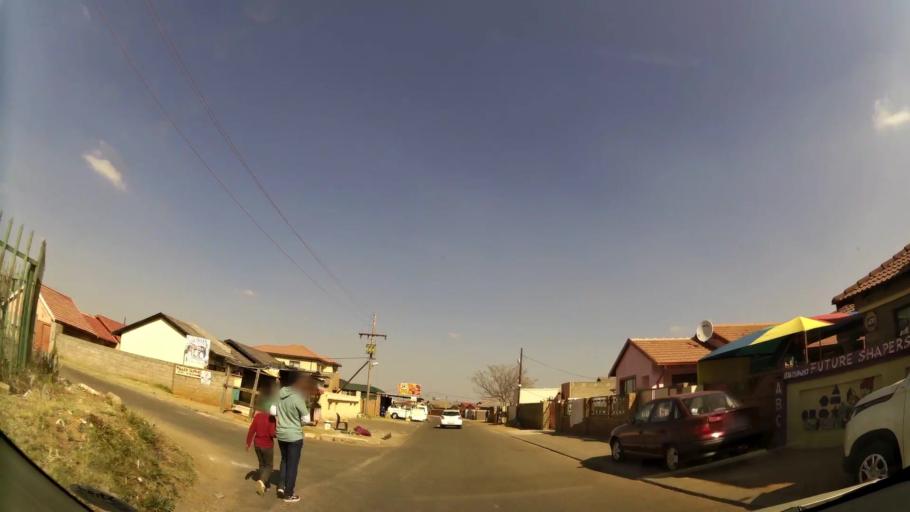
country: ZA
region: Gauteng
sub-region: City of Johannesburg Metropolitan Municipality
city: Roodepoort
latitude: -26.1653
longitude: 27.7972
